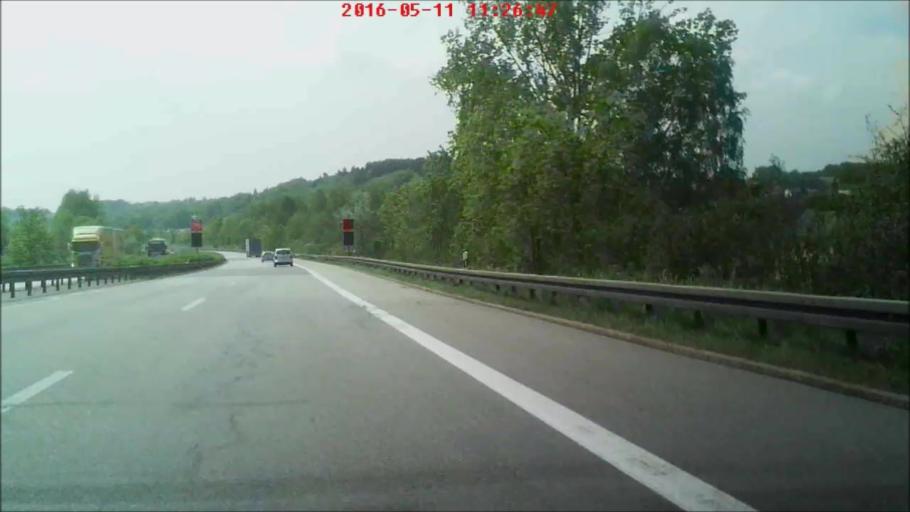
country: DE
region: Bavaria
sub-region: Upper Palatinate
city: Zeitlarn
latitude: 49.0742
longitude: 12.0980
